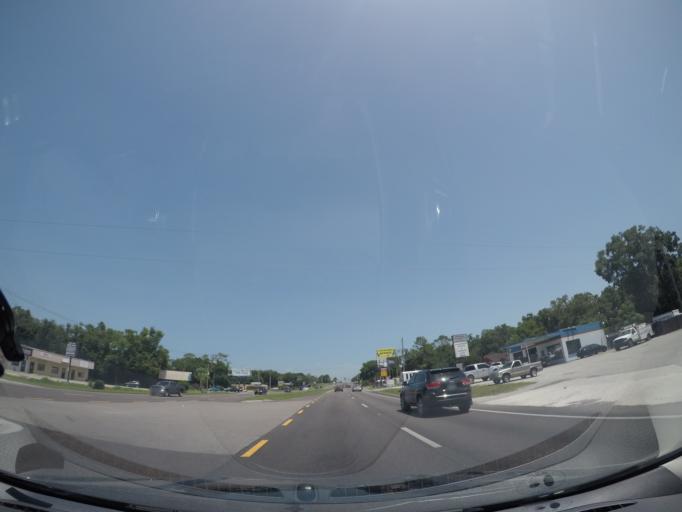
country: US
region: Florida
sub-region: Orange County
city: South Apopka
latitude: 28.6672
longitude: -81.4876
